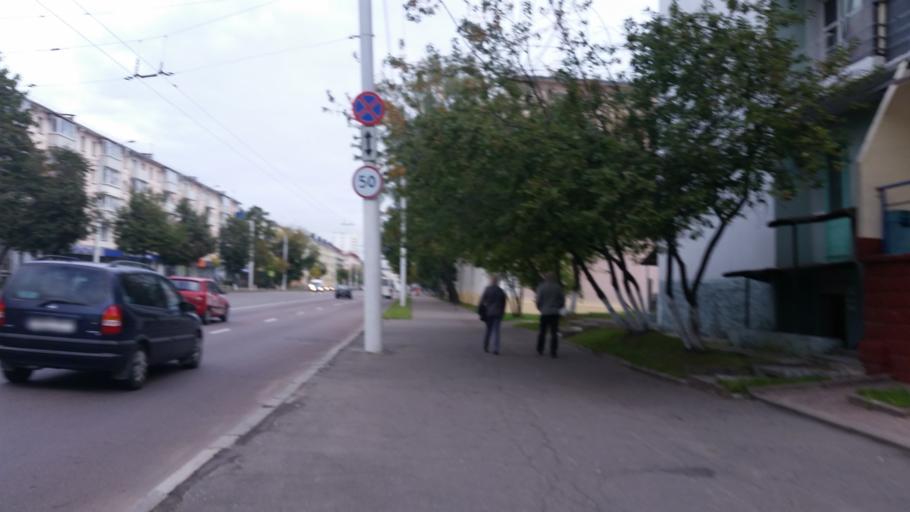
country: BY
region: Vitebsk
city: Vitebsk
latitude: 55.1755
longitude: 30.2005
